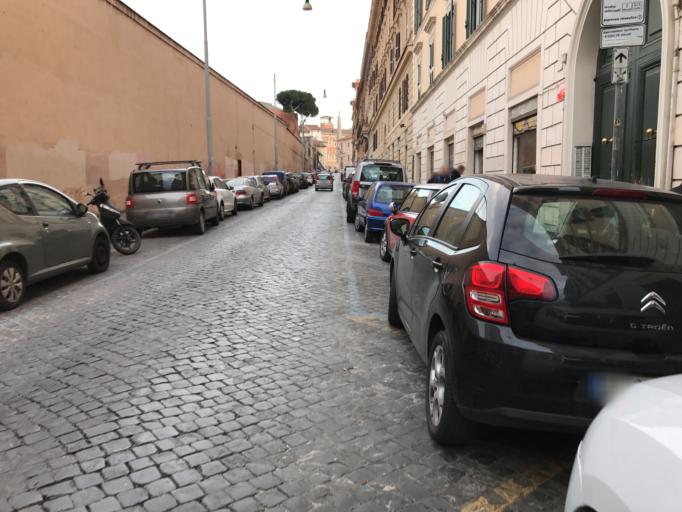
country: IT
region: Latium
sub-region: Citta metropolitana di Roma Capitale
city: Rome
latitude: 41.8882
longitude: 12.5003
